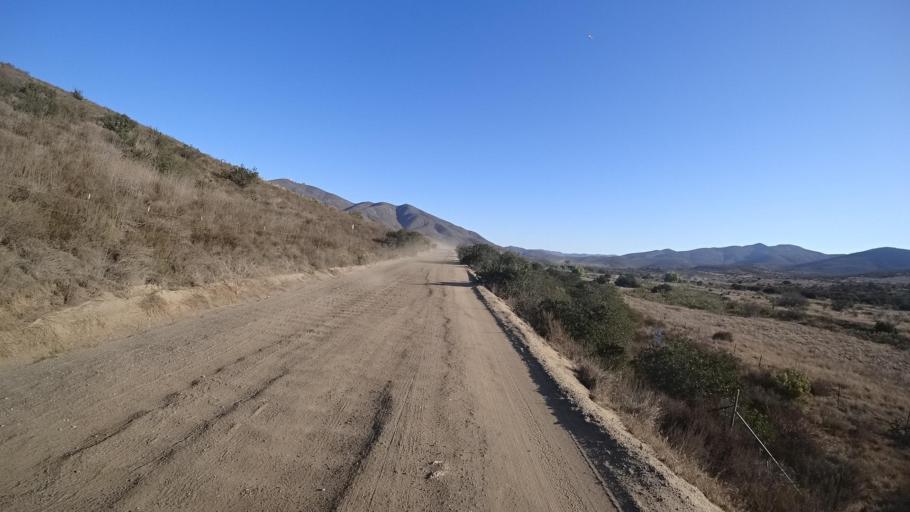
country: US
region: California
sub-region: San Diego County
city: Jamul
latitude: 32.6624
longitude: -116.9318
